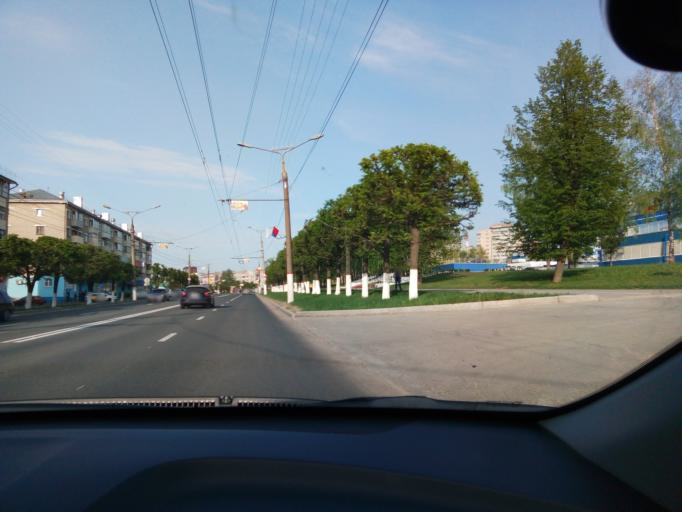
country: RU
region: Chuvashia
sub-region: Cheboksarskiy Rayon
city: Cheboksary
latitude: 56.1260
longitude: 47.2629
